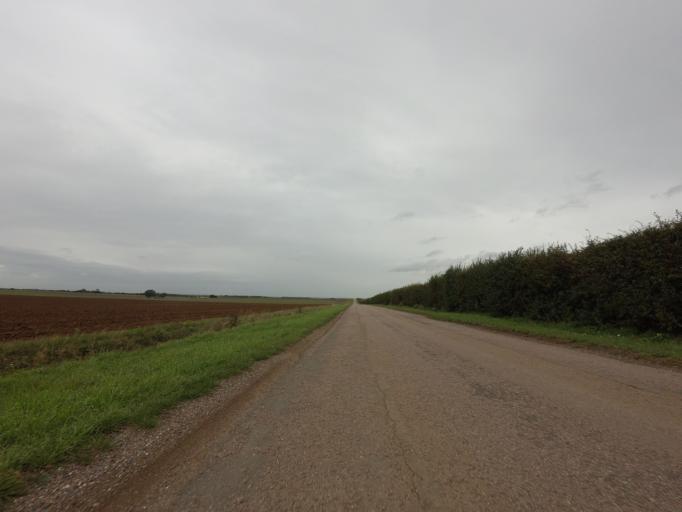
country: GB
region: England
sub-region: Cambridgeshire
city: Harston
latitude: 52.0700
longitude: 0.0937
